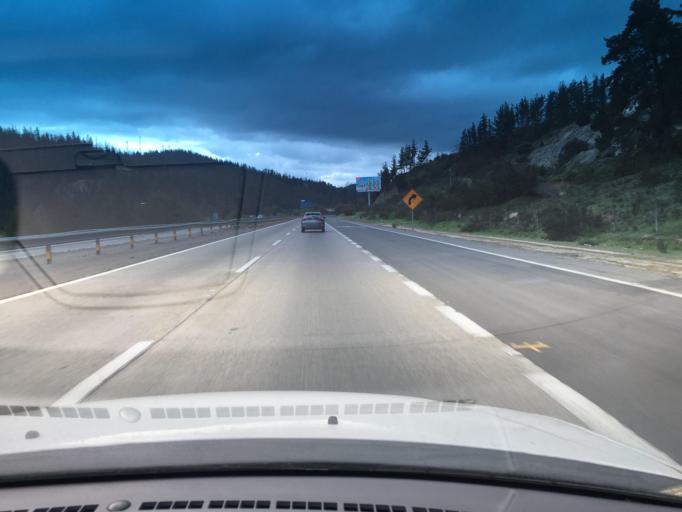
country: CL
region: Valparaiso
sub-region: Provincia de Marga Marga
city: Quilpue
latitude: -33.2301
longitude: -71.4654
